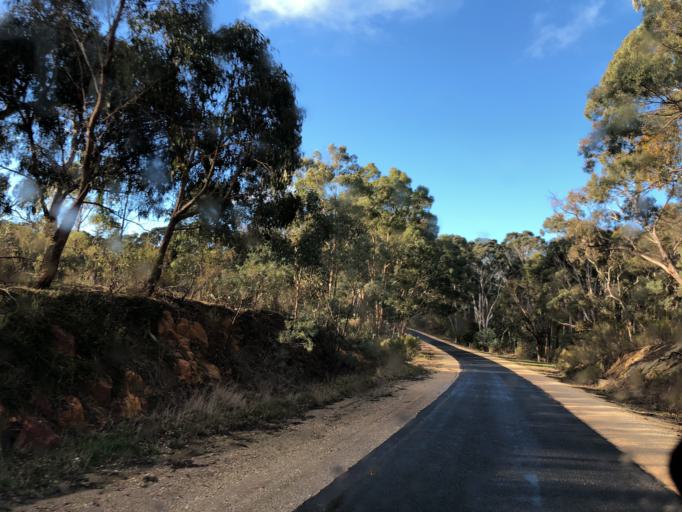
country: AU
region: Victoria
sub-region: Mount Alexander
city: Castlemaine
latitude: -37.2197
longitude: 144.2629
